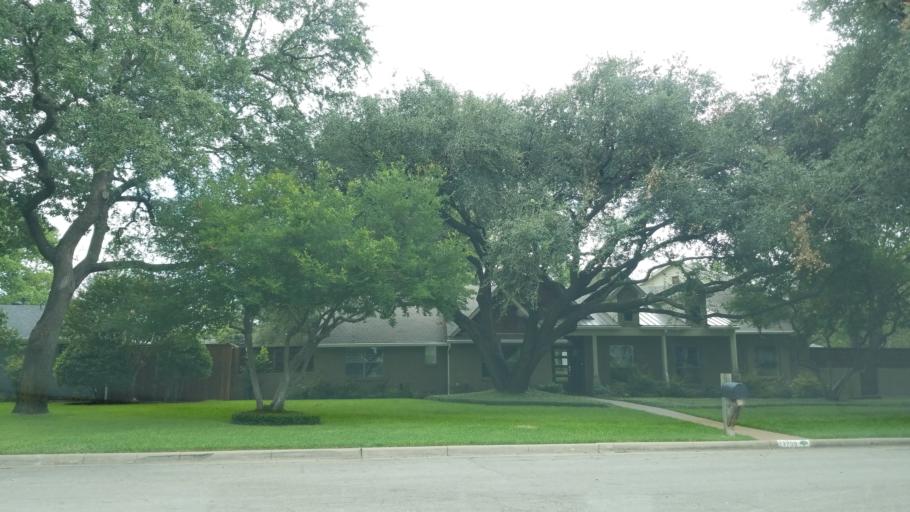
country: US
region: Texas
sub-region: Dallas County
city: Richardson
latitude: 32.9364
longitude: -96.7778
